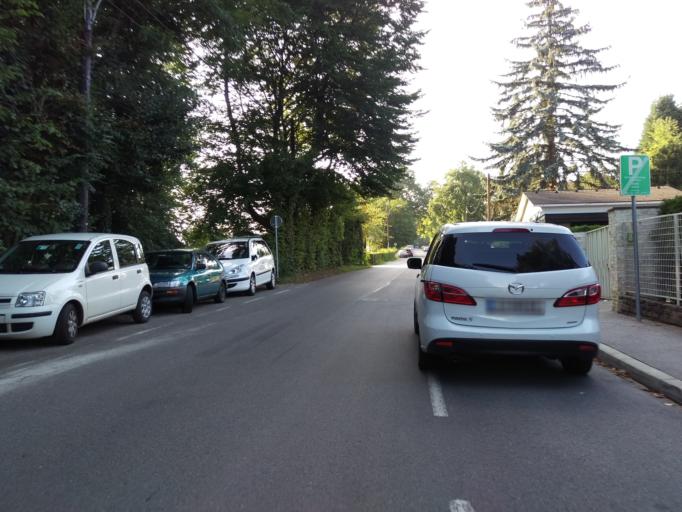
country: AT
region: Styria
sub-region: Graz Stadt
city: Graz
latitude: 47.0863
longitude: 15.4515
